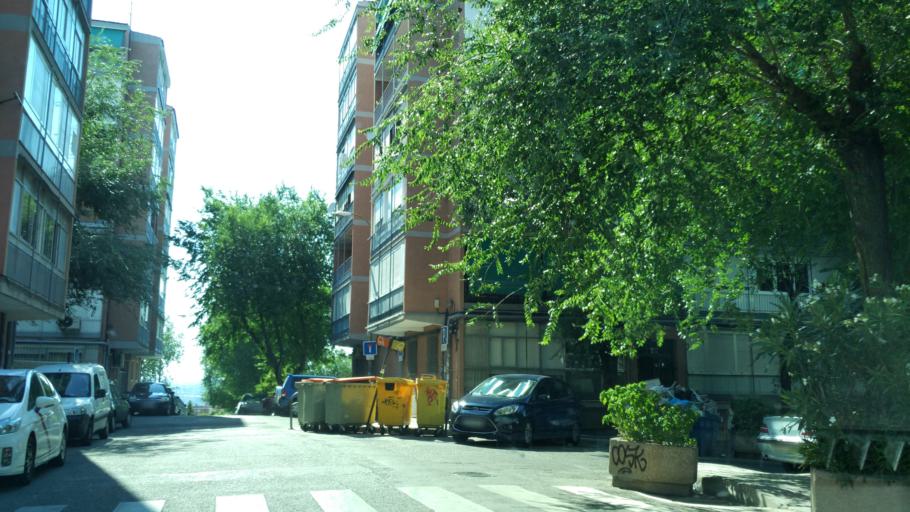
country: ES
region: Madrid
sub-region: Provincia de Madrid
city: Tetuan de las Victorias
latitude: 40.4634
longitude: -3.7186
